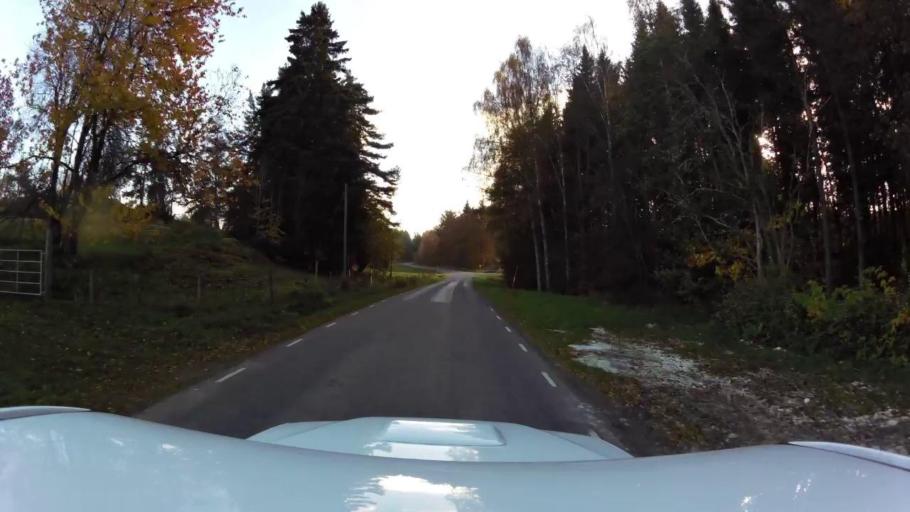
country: SE
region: OEstergoetland
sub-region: Linkopings Kommun
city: Vikingstad
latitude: 58.2740
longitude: 15.4364
